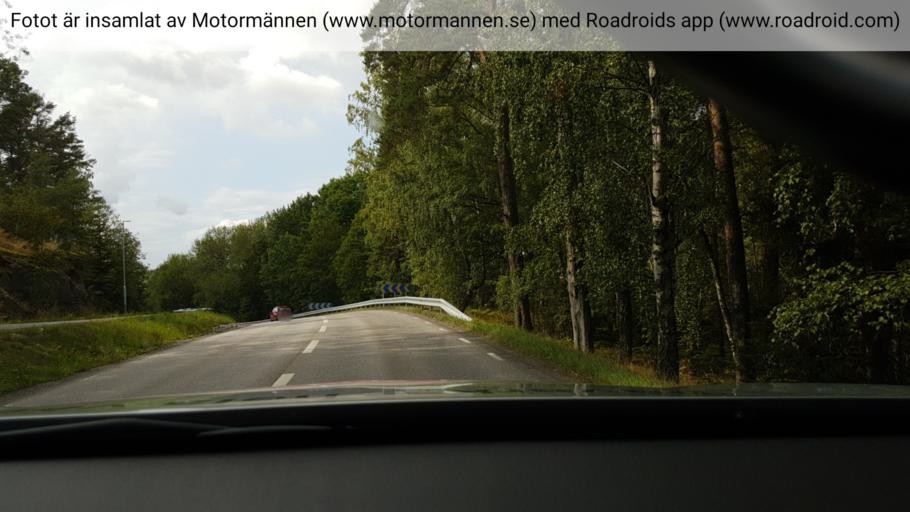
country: SE
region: Stockholm
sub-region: Ekero Kommun
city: Ekeroe
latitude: 59.3225
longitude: 17.7612
